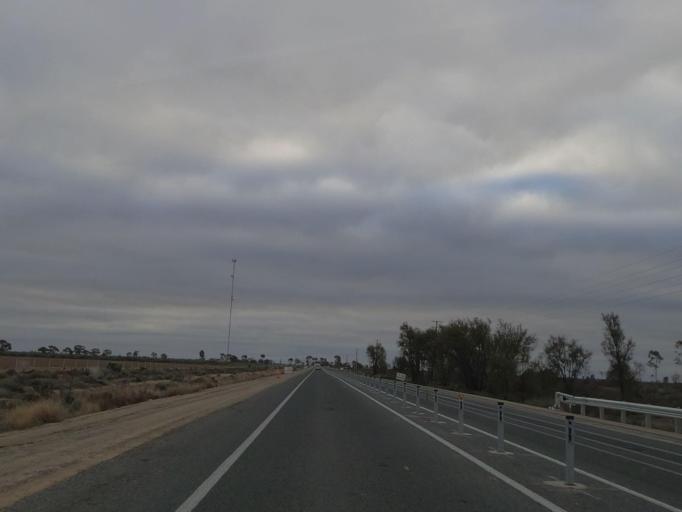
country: AU
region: Victoria
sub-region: Swan Hill
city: Swan Hill
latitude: -35.5309
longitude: 143.7402
